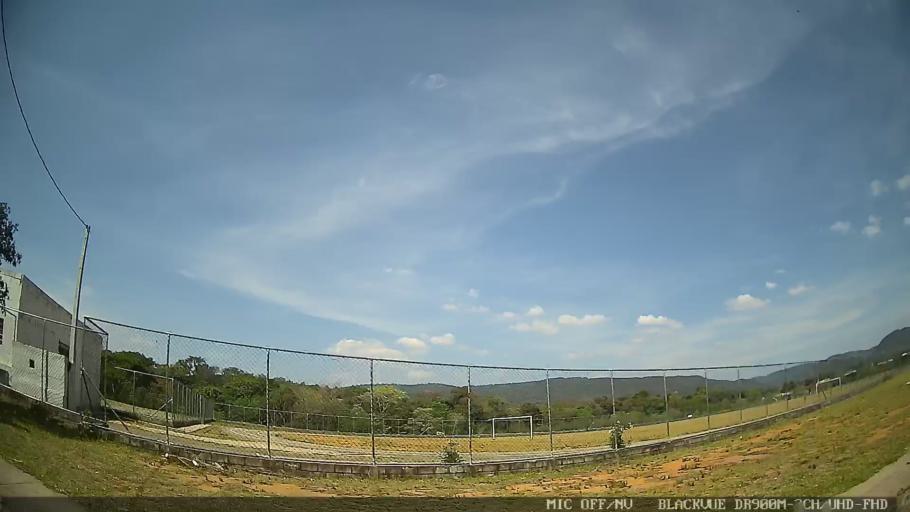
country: BR
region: Sao Paulo
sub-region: Cabreuva
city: Cabreuva
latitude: -23.2657
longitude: -47.0554
